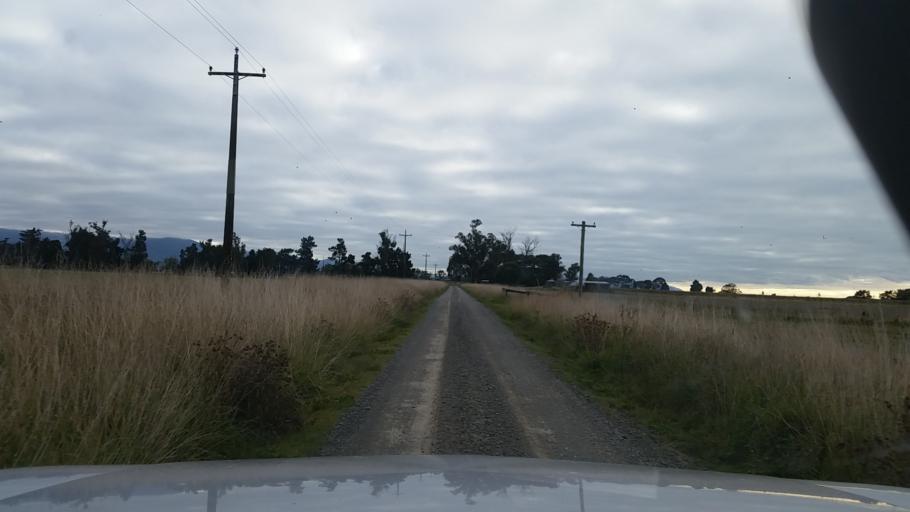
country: NZ
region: Marlborough
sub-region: Marlborough District
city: Blenheim
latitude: -41.5032
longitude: 174.0323
